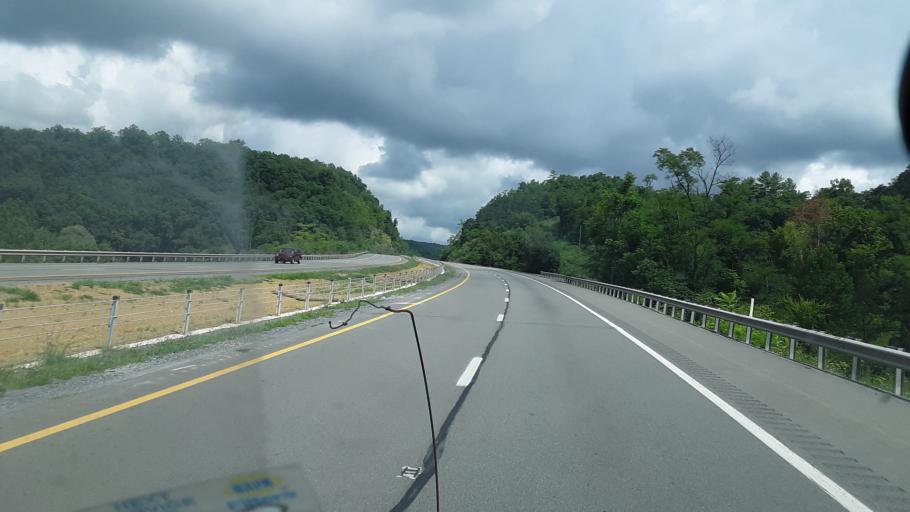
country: US
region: West Virginia
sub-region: Greenbrier County
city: Lewisburg
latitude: 37.7821
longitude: -80.3817
